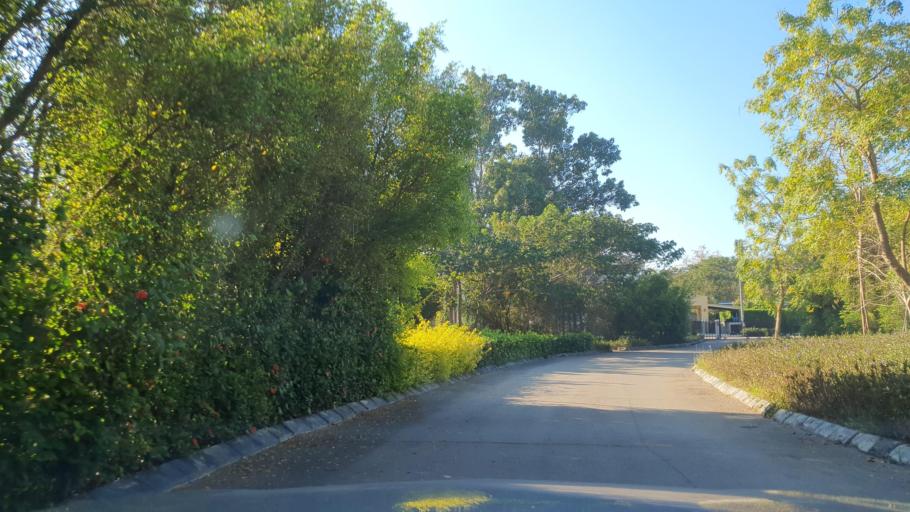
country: TH
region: Chiang Mai
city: Hang Dong
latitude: 18.6934
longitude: 98.9587
